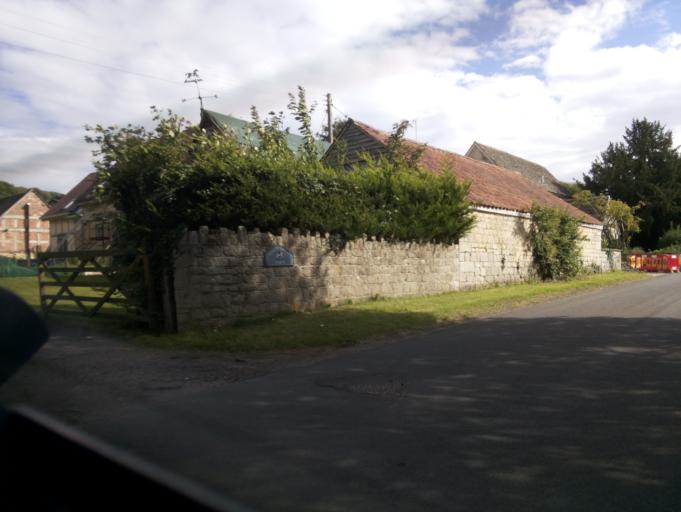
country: GB
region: England
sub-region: Gloucestershire
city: Stonehouse
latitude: 51.7859
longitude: -2.2760
